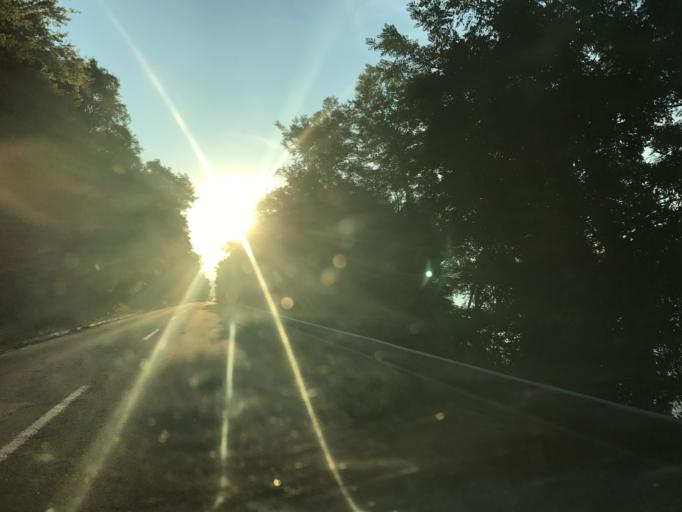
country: RO
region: Caras-Severin
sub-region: Comuna Berzasca
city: Liubcova
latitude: 44.6409
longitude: 21.8981
